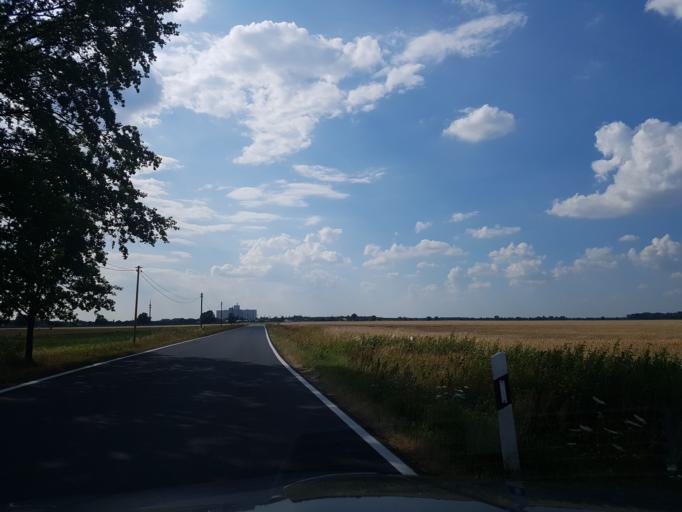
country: DE
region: Brandenburg
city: Herzberg
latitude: 51.6879
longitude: 13.2830
